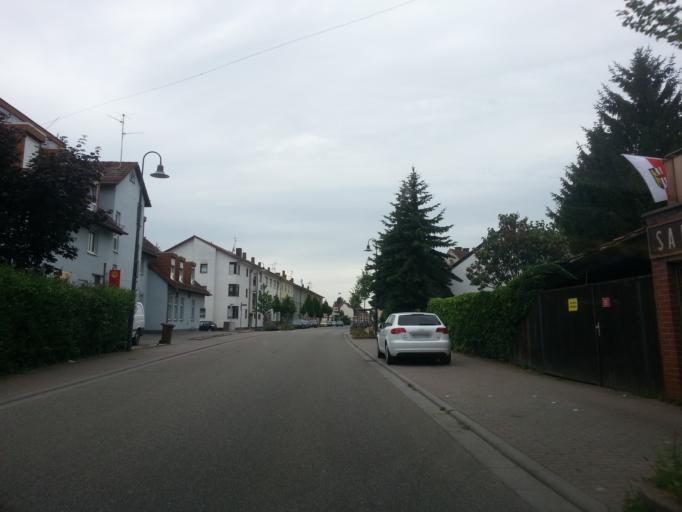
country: DE
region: Baden-Wuerttemberg
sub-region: Karlsruhe Region
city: Edingen-Neckarhausen
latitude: 49.4495
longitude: 8.6103
